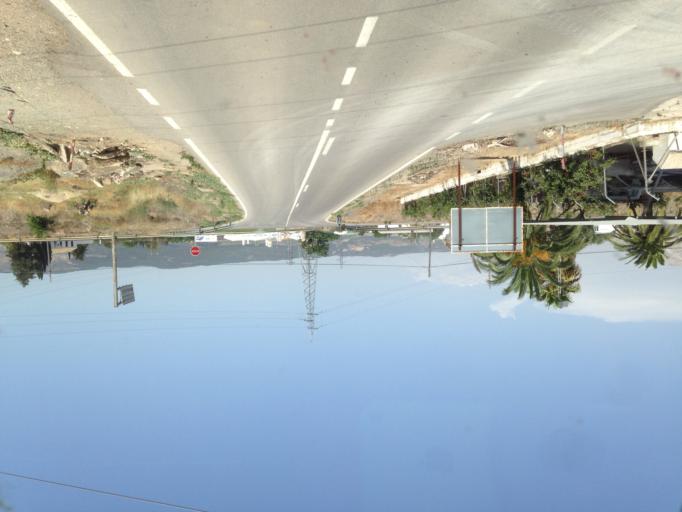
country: ES
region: Andalusia
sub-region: Provincia de Malaga
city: Antequera
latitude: 37.0533
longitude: -4.5636
